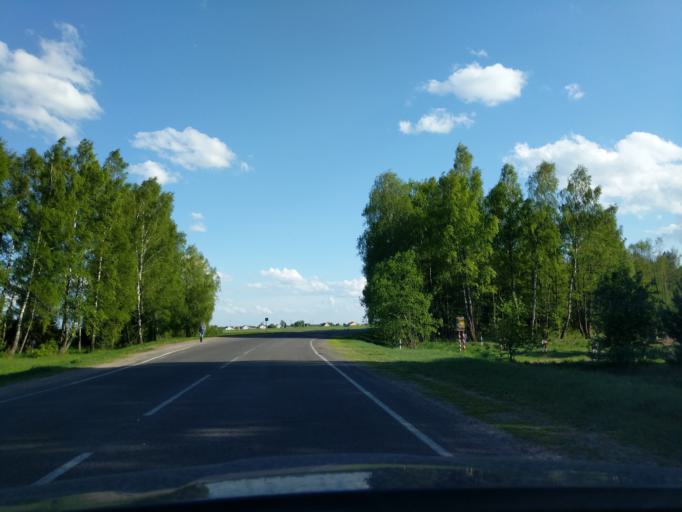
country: BY
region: Minsk
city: Kryvichy
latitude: 54.6963
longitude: 27.1550
